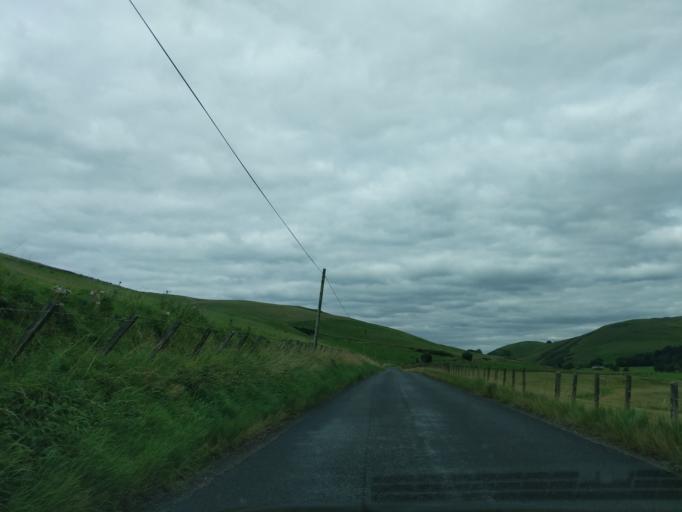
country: GB
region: Scotland
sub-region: The Scottish Borders
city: West Linton
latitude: 55.6813
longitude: -3.3336
